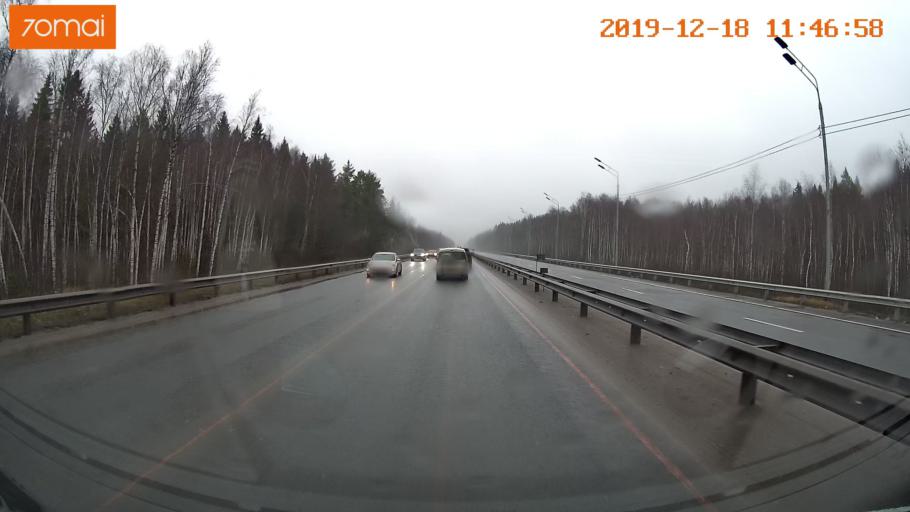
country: RU
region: Moskovskaya
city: Yershovo
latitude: 55.7532
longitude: 36.8908
